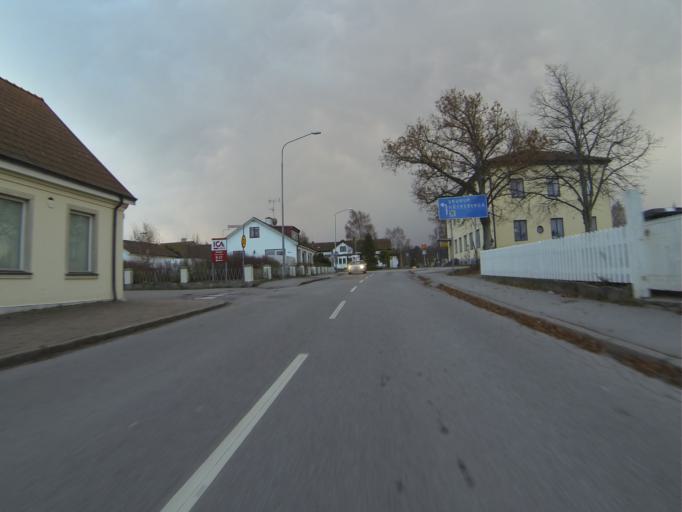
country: SE
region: Skane
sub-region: Lunds Kommun
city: Genarp
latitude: 55.6004
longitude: 13.4008
